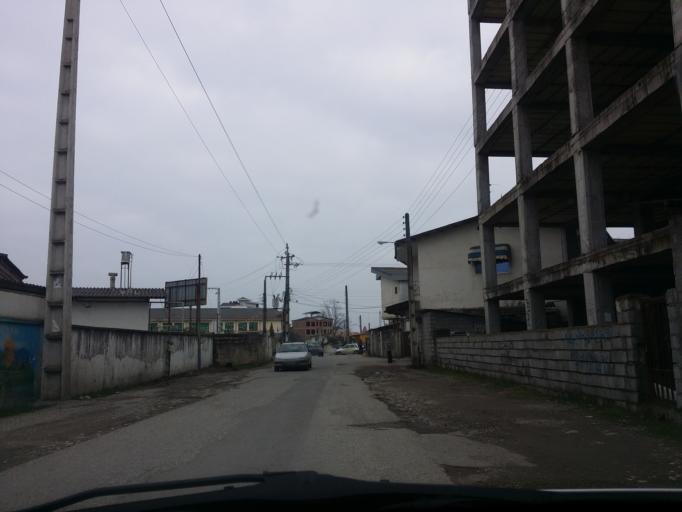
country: IR
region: Mazandaran
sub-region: Nowshahr
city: Nowshahr
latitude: 36.6436
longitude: 51.4804
